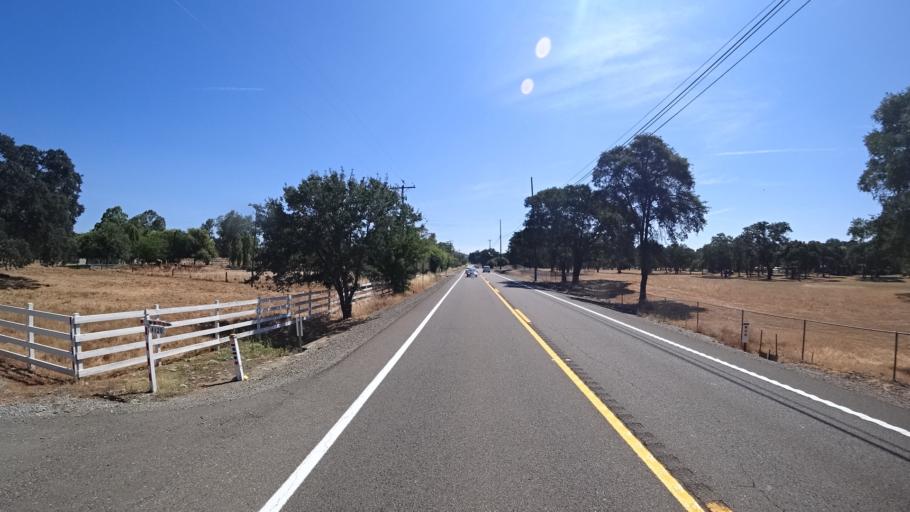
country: US
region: California
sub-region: Calaveras County
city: Rancho Calaveras
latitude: 38.1809
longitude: -120.9084
